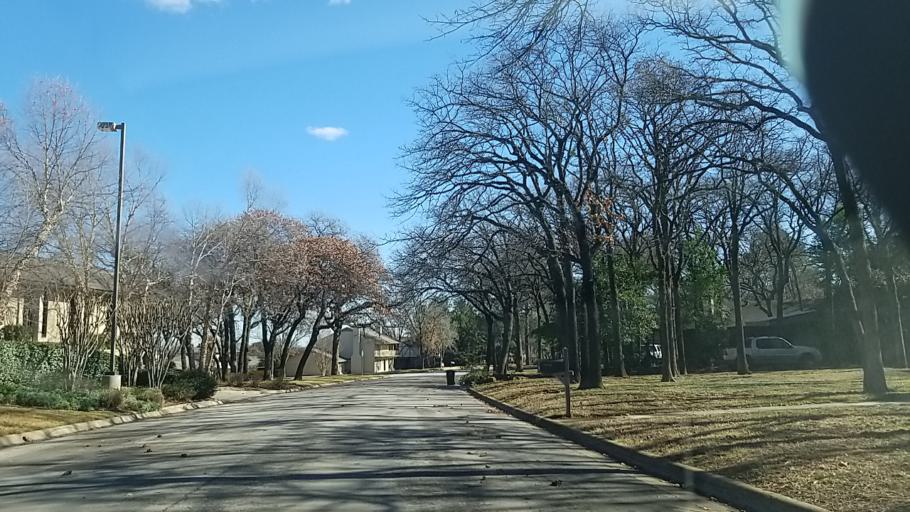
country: US
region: Texas
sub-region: Denton County
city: Denton
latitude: 33.1907
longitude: -97.1186
